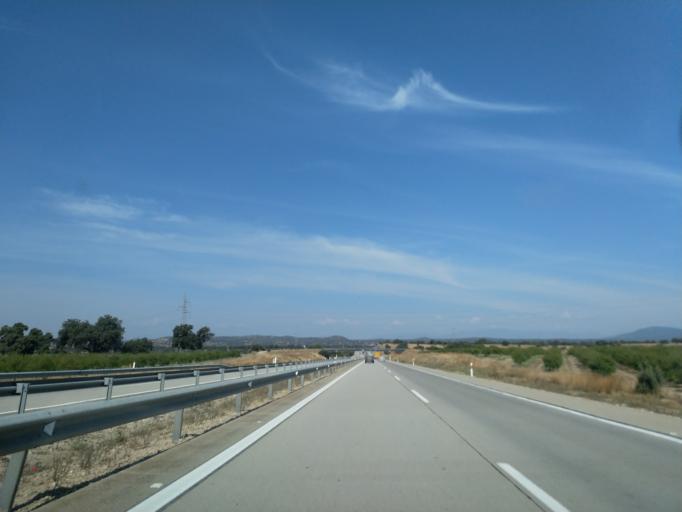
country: ES
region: Castille-La Mancha
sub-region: Province of Toledo
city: Cervera de los Montes
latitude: 39.9978
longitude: -4.7647
